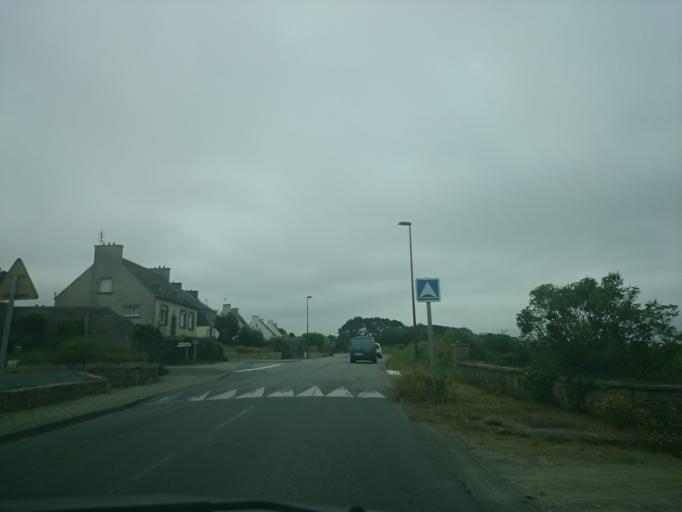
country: FR
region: Brittany
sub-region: Departement du Finistere
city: Lannilis
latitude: 48.5522
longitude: -4.5410
